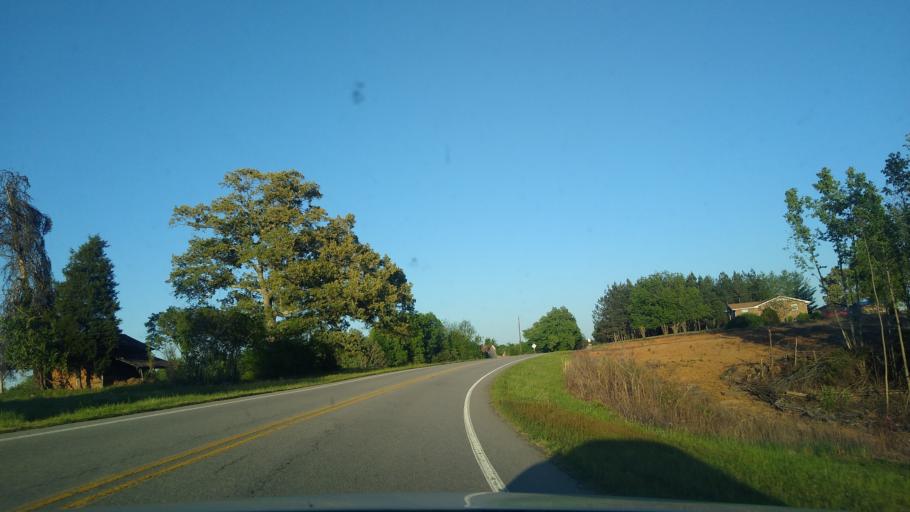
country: US
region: North Carolina
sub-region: Rockingham County
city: Reidsville
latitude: 36.3789
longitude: -79.5900
